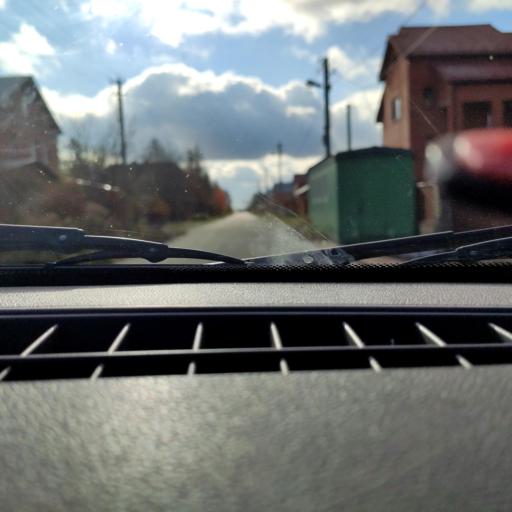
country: RU
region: Bashkortostan
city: Ufa
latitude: 54.5986
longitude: 55.9340
